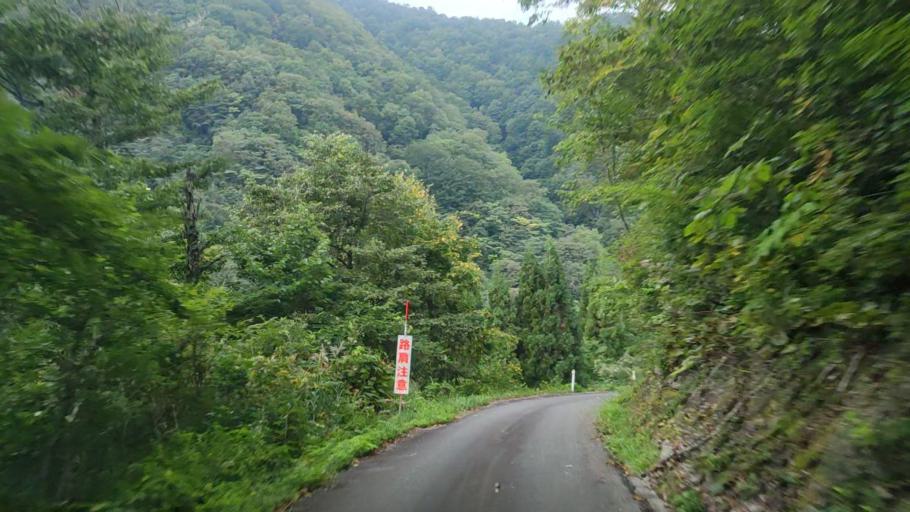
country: JP
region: Toyama
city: Yatsuomachi-higashikumisaka
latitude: 36.4017
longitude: 137.0744
